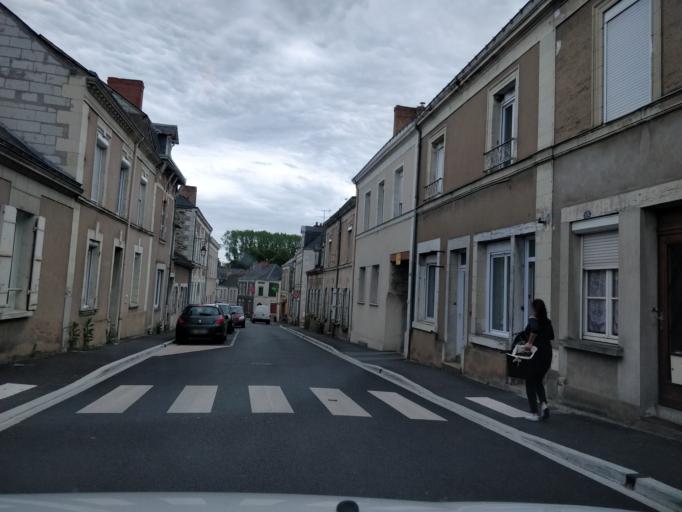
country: FR
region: Pays de la Loire
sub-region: Departement de Maine-et-Loire
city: Feneu
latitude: 47.5716
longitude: -0.5929
